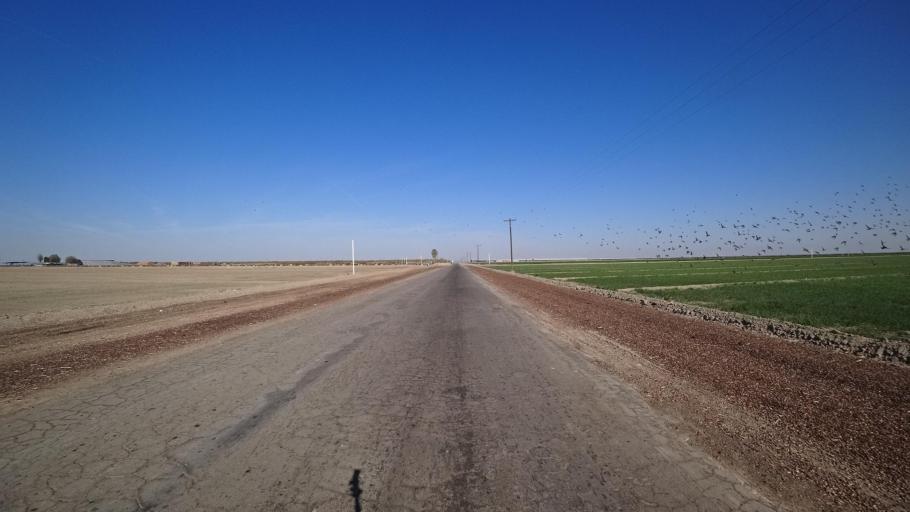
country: US
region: California
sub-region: Kern County
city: Wasco
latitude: 35.7233
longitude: -119.4193
